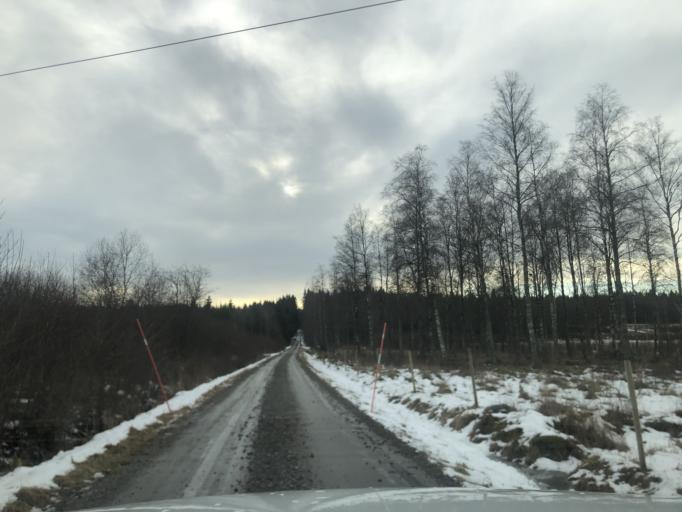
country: SE
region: Vaestra Goetaland
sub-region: Ulricehamns Kommun
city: Ulricehamn
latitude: 57.7891
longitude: 13.4840
